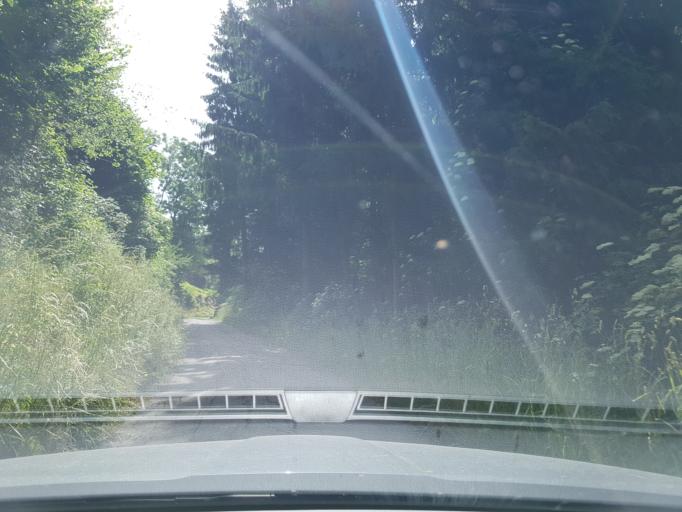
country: AT
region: Carinthia
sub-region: Politischer Bezirk Spittal an der Drau
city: Millstatt
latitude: 46.7814
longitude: 13.5560
